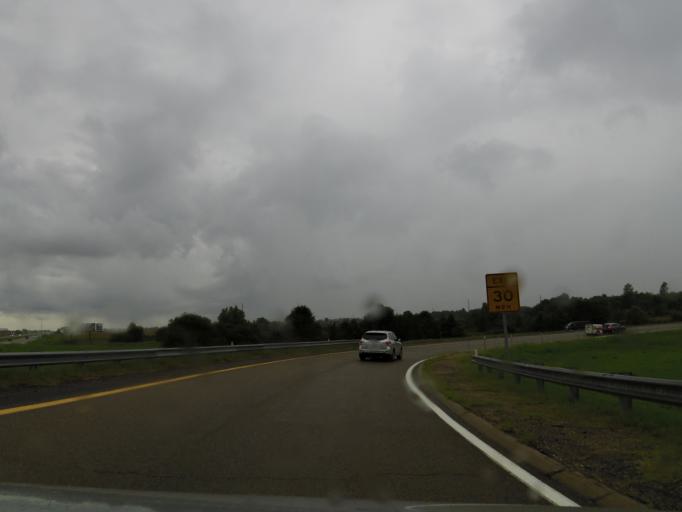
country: US
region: Missouri
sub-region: Scott County
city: Sikeston
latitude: 36.8720
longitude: -89.5334
